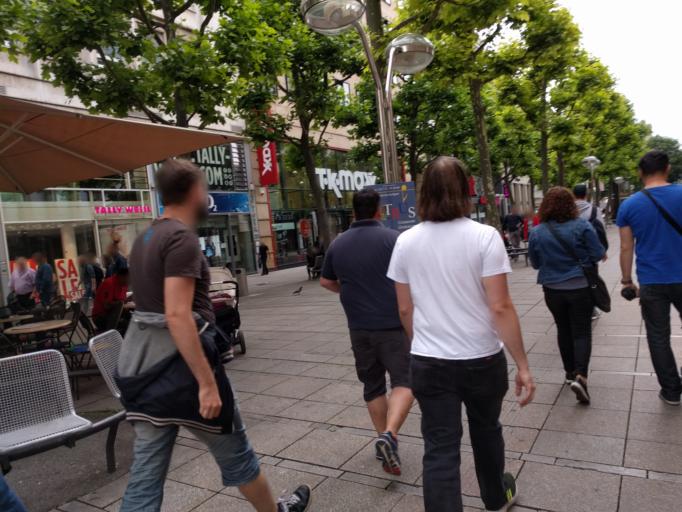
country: DE
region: Baden-Wuerttemberg
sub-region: Regierungsbezirk Stuttgart
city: Stuttgart
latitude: 48.7799
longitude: 9.1796
